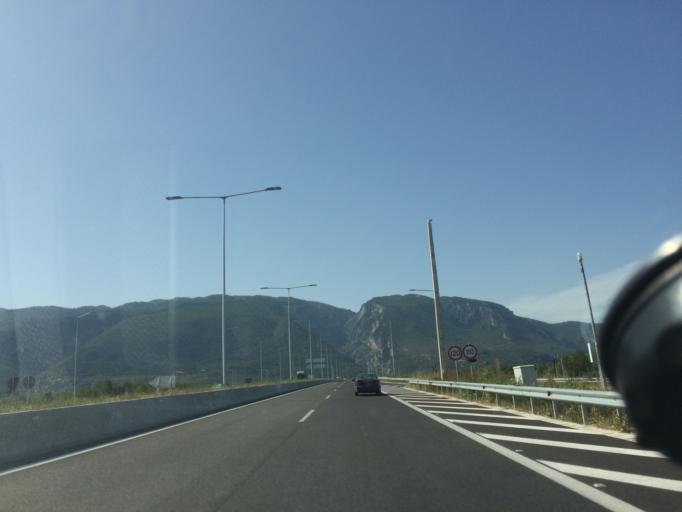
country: GR
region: Thessaly
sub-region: Nomos Larisis
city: Pyrgetos
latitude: 39.9084
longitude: 22.6249
